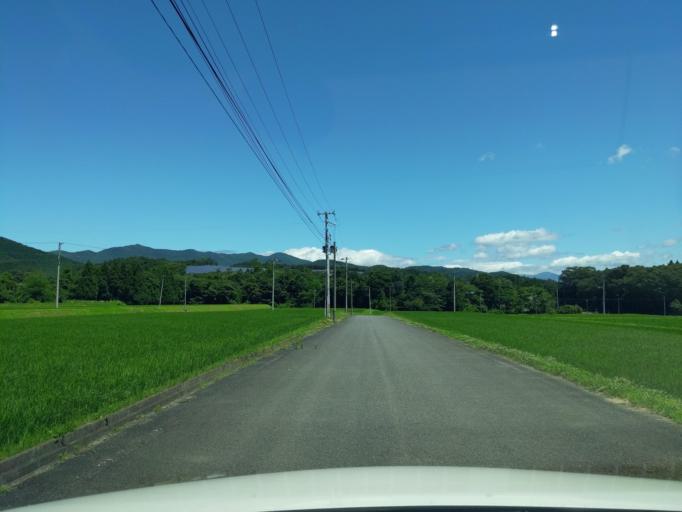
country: JP
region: Fukushima
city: Koriyama
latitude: 37.3898
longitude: 140.2460
